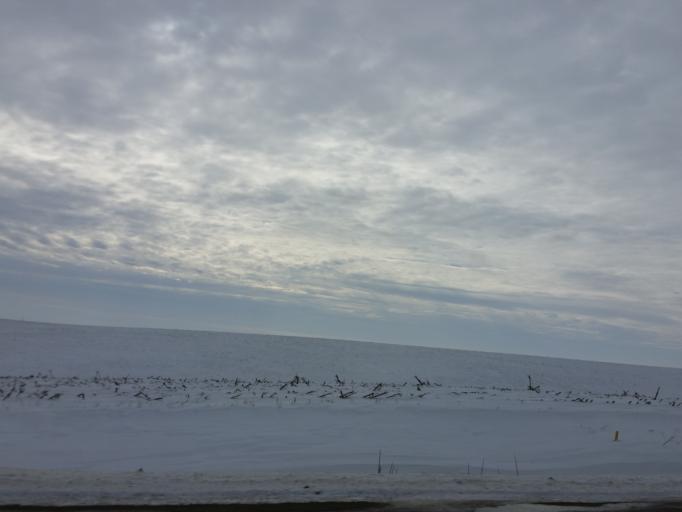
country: US
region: Iowa
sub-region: Dubuque County
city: Peosta
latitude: 42.3821
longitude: -90.7673
